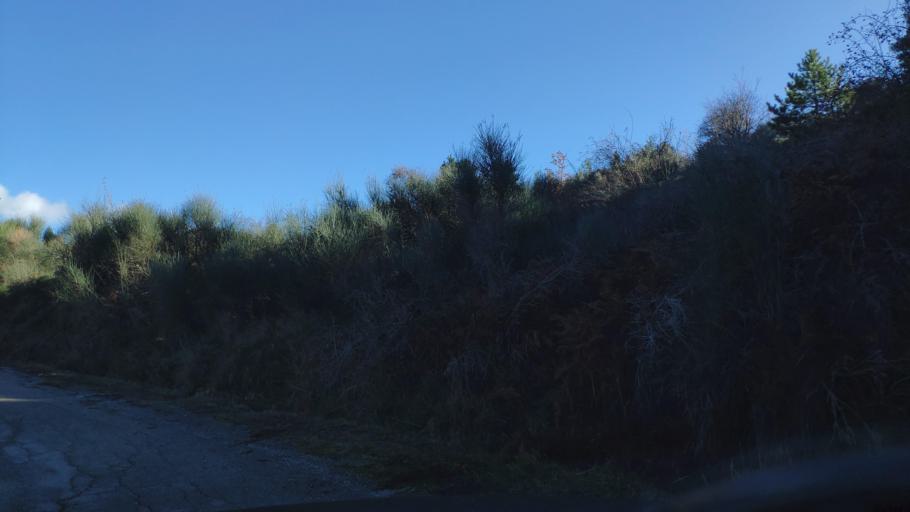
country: GR
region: West Greece
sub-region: Nomos Achaias
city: Aiyira
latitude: 38.0445
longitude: 22.4542
